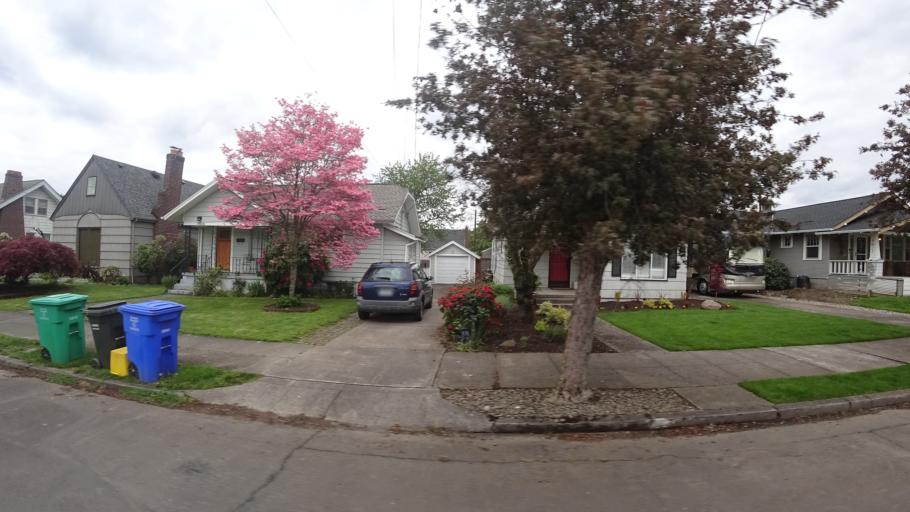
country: US
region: Oregon
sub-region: Clackamas County
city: Milwaukie
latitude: 45.4765
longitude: -122.6451
